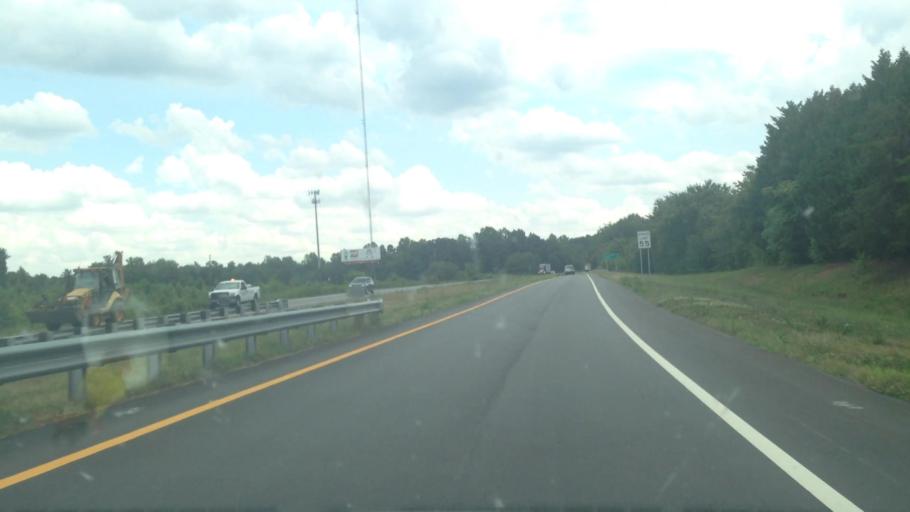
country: US
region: North Carolina
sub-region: Guilford County
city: Stokesdale
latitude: 36.2830
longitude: -79.9403
